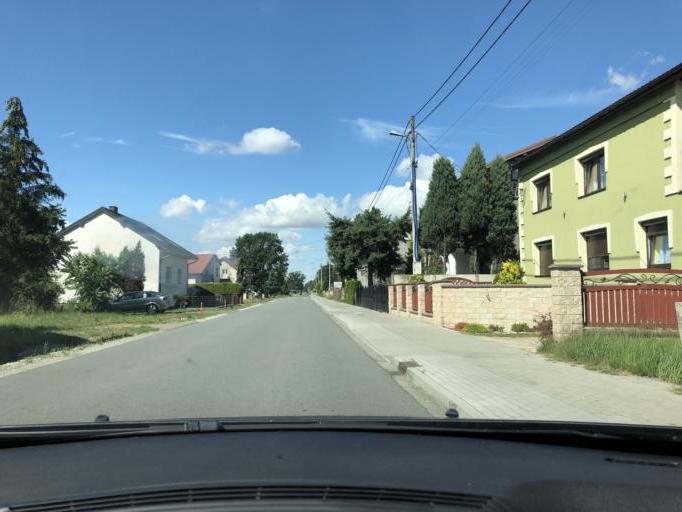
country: PL
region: Lodz Voivodeship
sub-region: Powiat wieruszowski
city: Czastary
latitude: 51.2417
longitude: 18.3226
